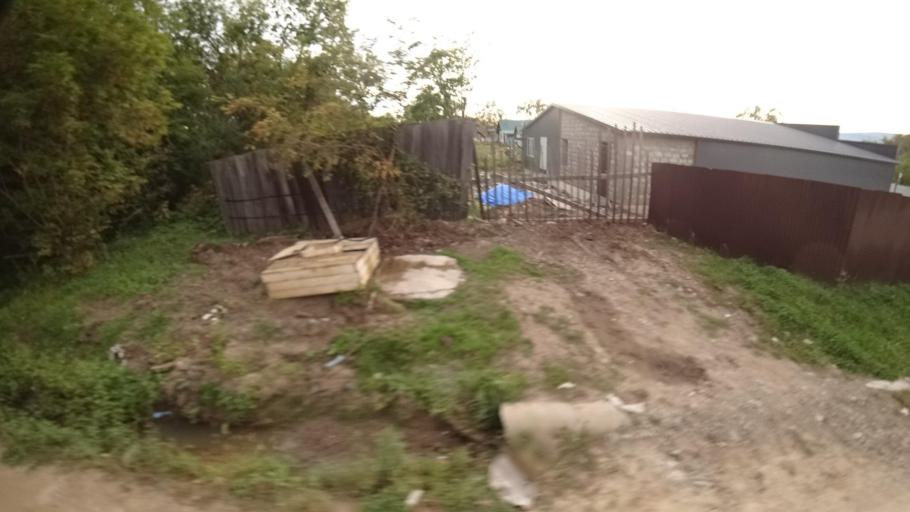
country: RU
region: Primorskiy
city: Yakovlevka
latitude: 44.4222
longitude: 133.4613
